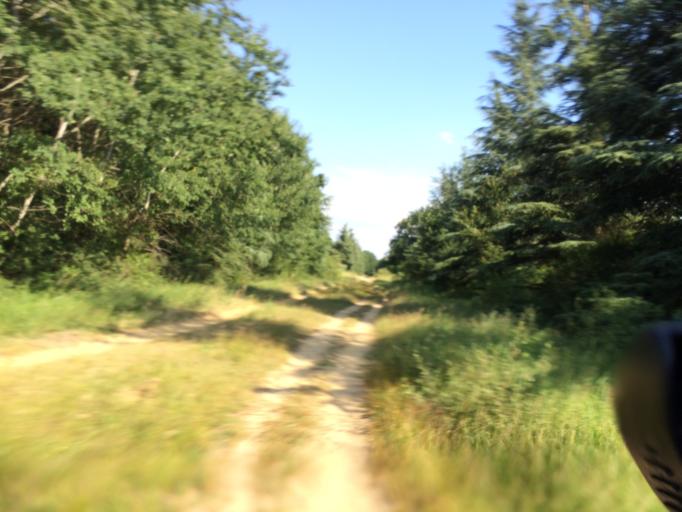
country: FR
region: Ile-de-France
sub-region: Departement de l'Essonne
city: Soisy-sur-Seine
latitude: 48.6766
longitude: 2.4508
